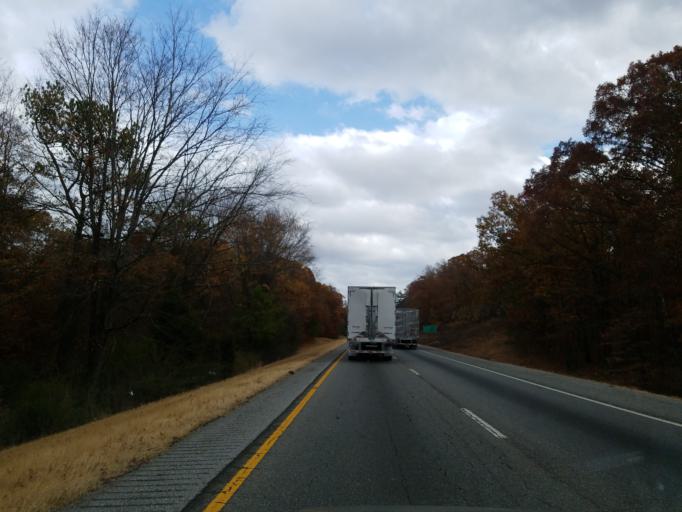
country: US
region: Alabama
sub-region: Talladega County
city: Lincoln
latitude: 33.5898
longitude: -86.1125
